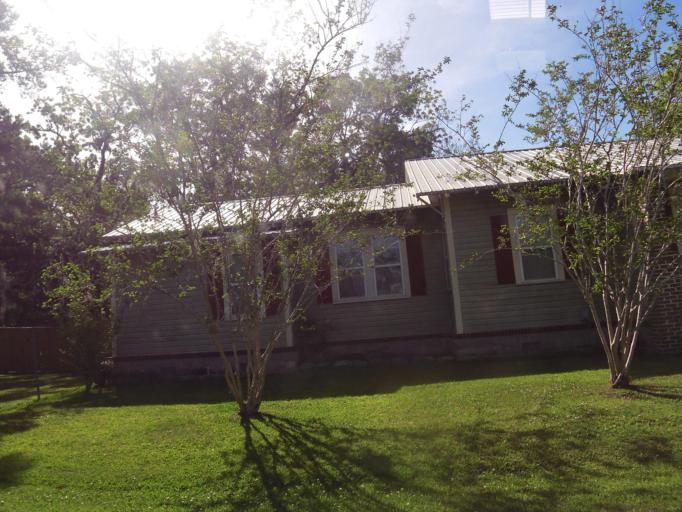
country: US
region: Florida
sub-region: Nassau County
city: Callahan
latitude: 30.5627
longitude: -81.8324
